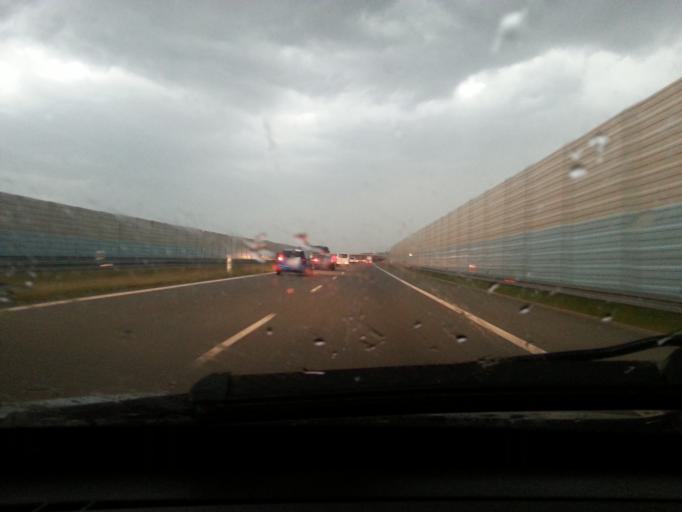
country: PL
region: Lodz Voivodeship
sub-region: powiat Lowicki
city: Lyszkowice
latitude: 51.9686
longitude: 19.8650
